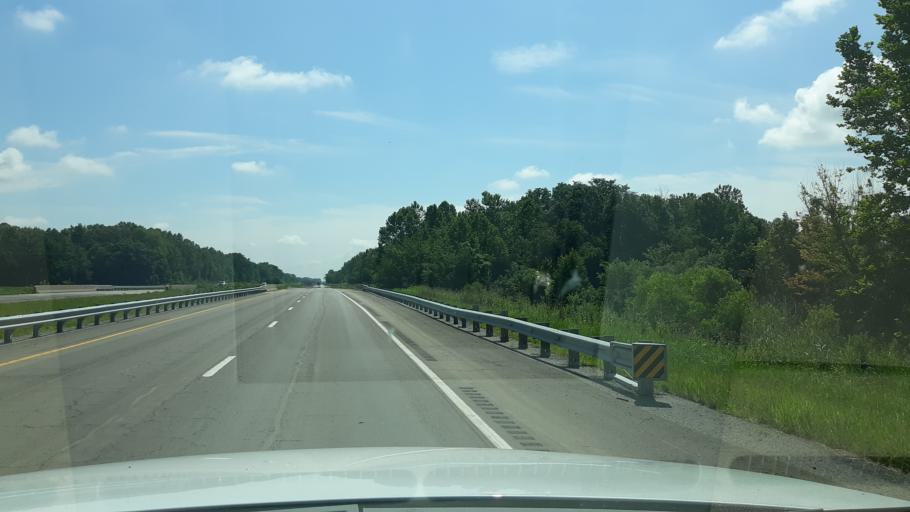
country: US
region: Illinois
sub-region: Saline County
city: Carrier Mills
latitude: 37.7333
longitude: -88.6702
